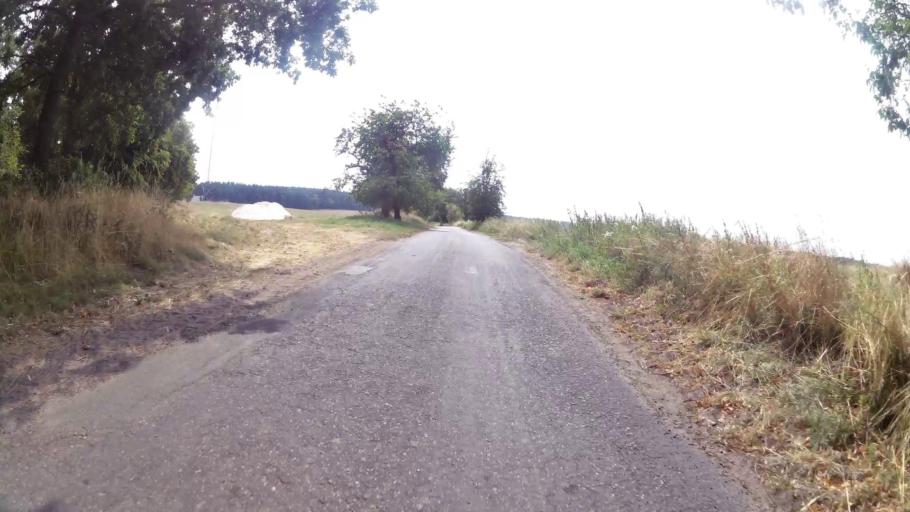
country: PL
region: West Pomeranian Voivodeship
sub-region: Powiat gryfinski
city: Mieszkowice
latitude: 52.8821
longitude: 14.5279
